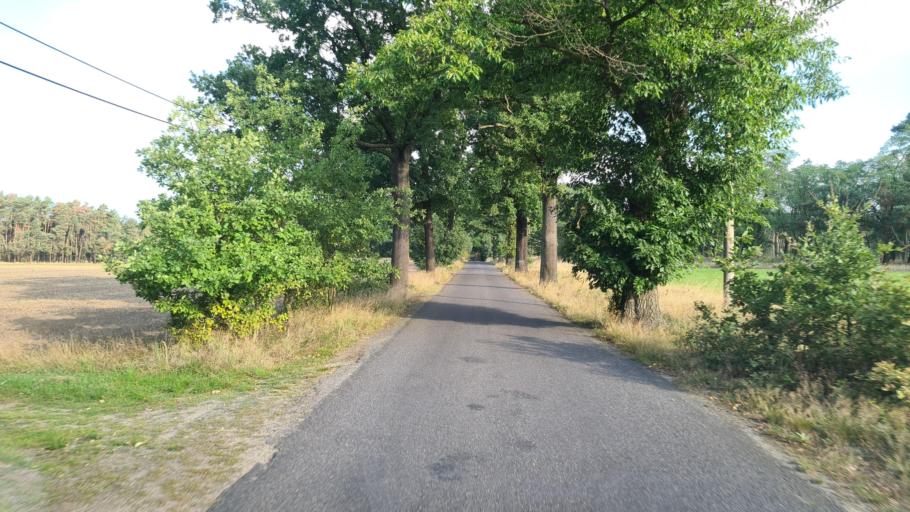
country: DE
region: Brandenburg
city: Neupetershain
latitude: 51.6252
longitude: 14.1027
